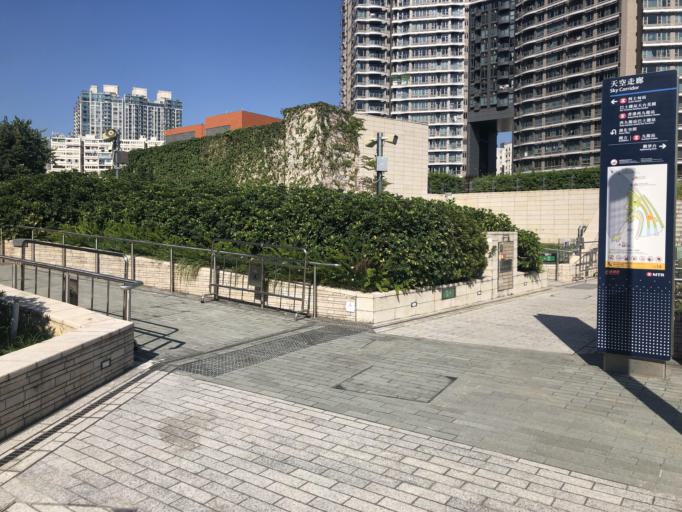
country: HK
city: Hong Kong
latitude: 22.3046
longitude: 114.1655
